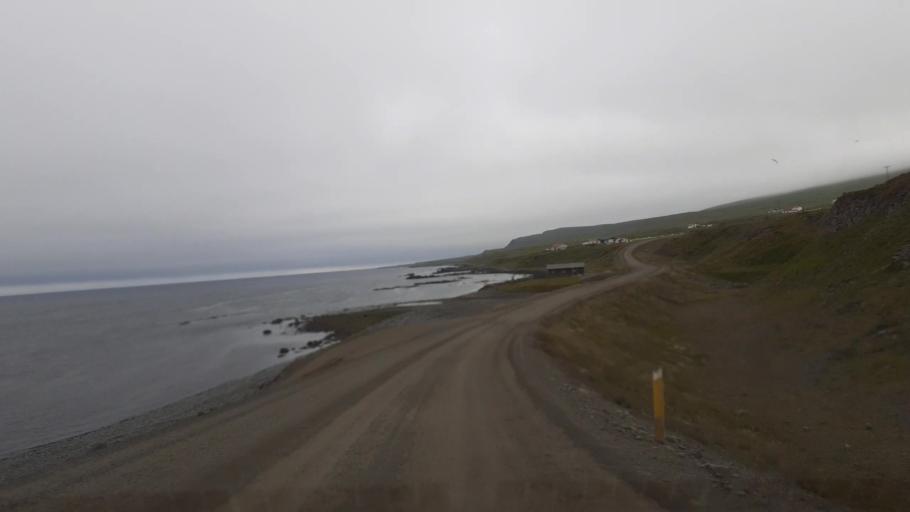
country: IS
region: Northwest
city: Saudarkrokur
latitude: 65.5267
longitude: -20.9639
